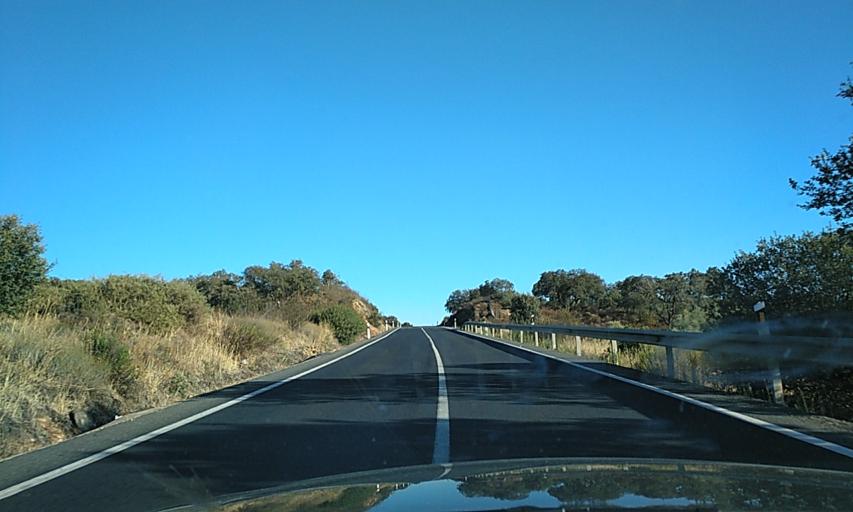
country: ES
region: Andalusia
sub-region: Provincia de Huelva
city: Alosno
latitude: 37.5225
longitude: -7.1355
